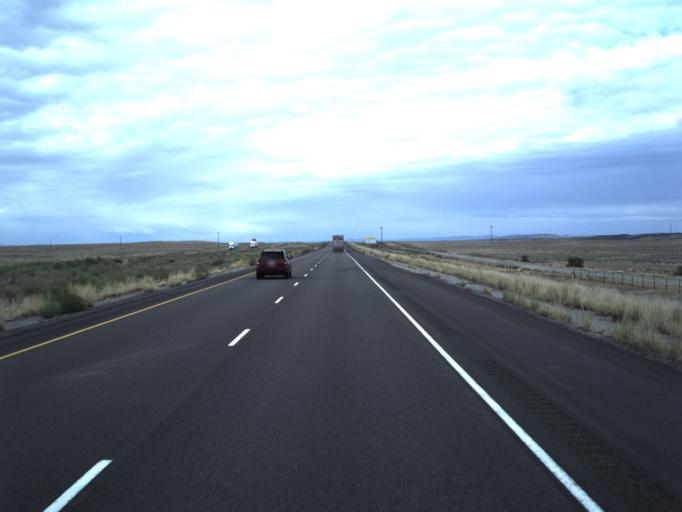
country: US
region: Colorado
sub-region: Mesa County
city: Loma
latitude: 39.0464
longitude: -109.2714
